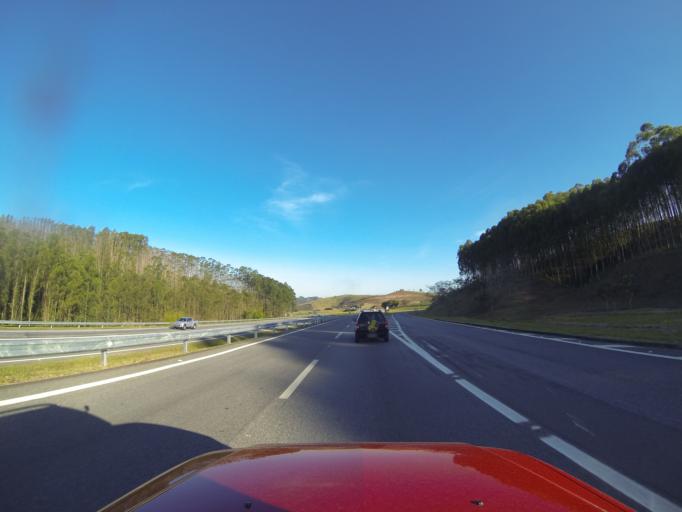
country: BR
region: Sao Paulo
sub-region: Jacarei
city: Jacarei
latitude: -23.3401
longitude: -46.0234
